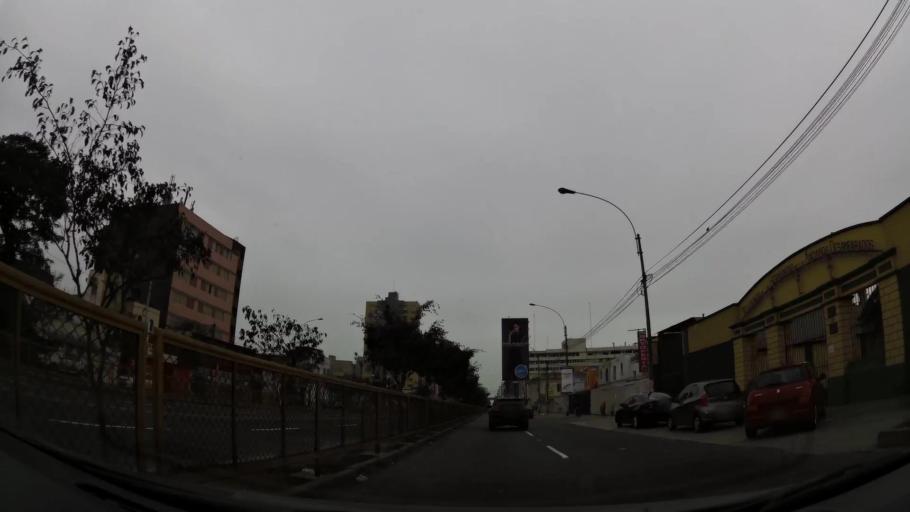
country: PE
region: Lima
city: Lima
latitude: -12.0638
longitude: -77.0446
